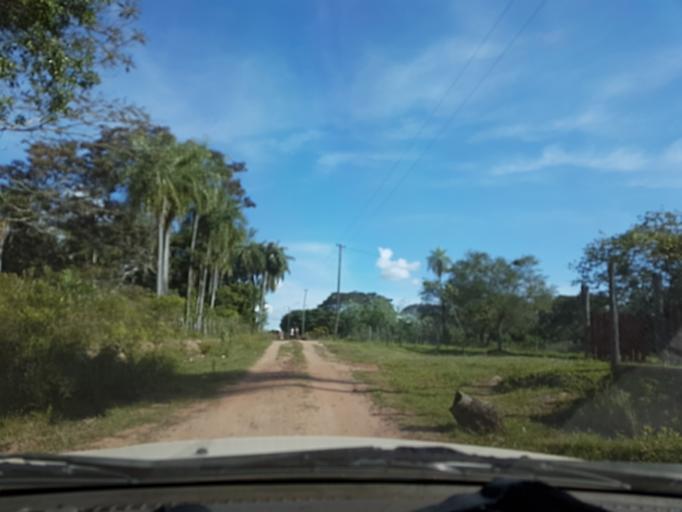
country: PY
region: Cordillera
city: Arroyos y Esteros
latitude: -24.9765
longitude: -57.1946
